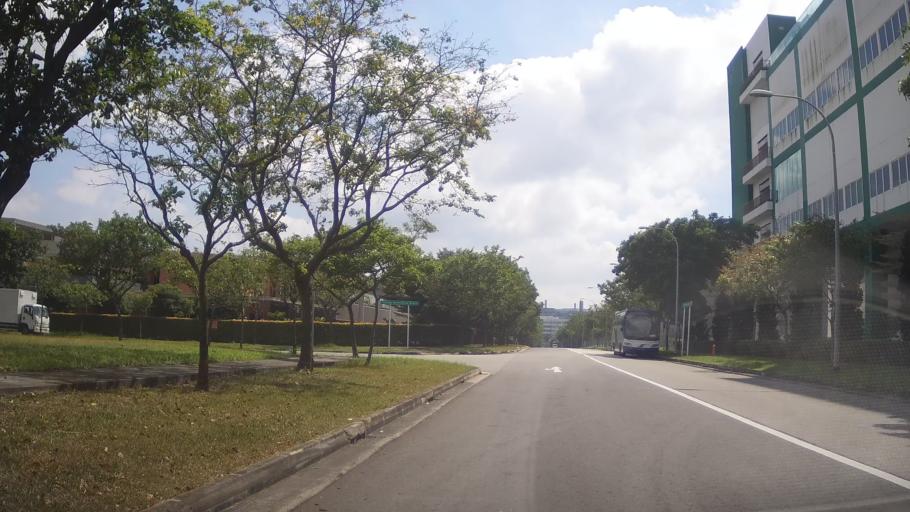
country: SG
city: Singapore
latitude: 1.3228
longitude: 103.7113
